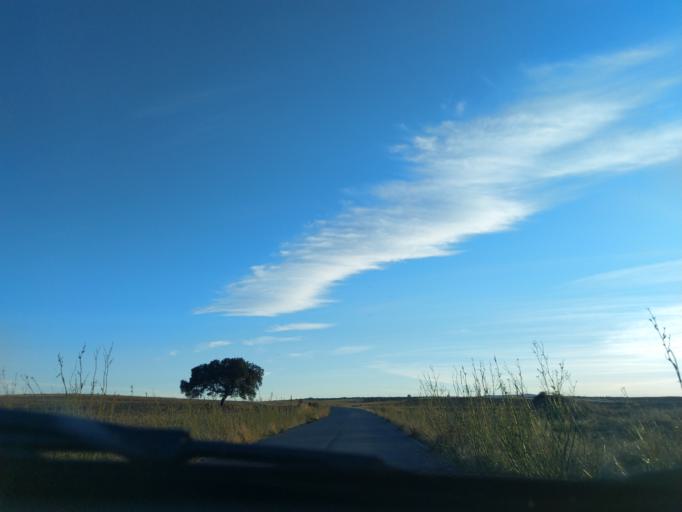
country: ES
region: Extremadura
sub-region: Provincia de Badajoz
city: Valverde de Llerena
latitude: 38.2316
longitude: -5.8227
